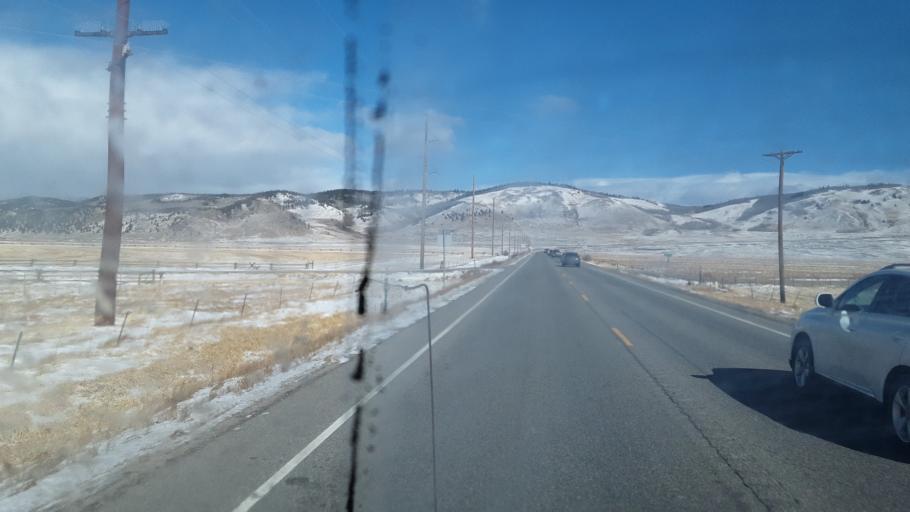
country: US
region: Colorado
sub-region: Summit County
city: Breckenridge
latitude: 39.3910
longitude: -105.7873
